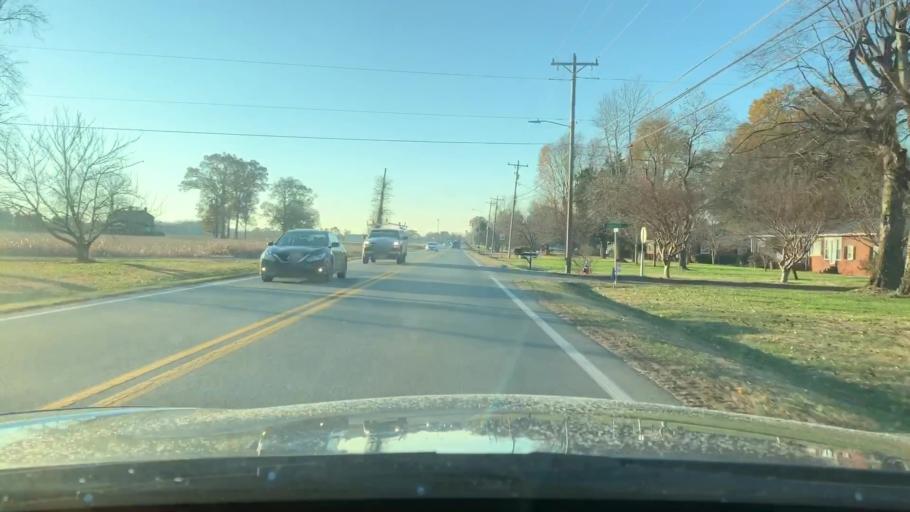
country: US
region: North Carolina
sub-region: Alamance County
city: Green Level
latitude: 36.1101
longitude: -79.3534
